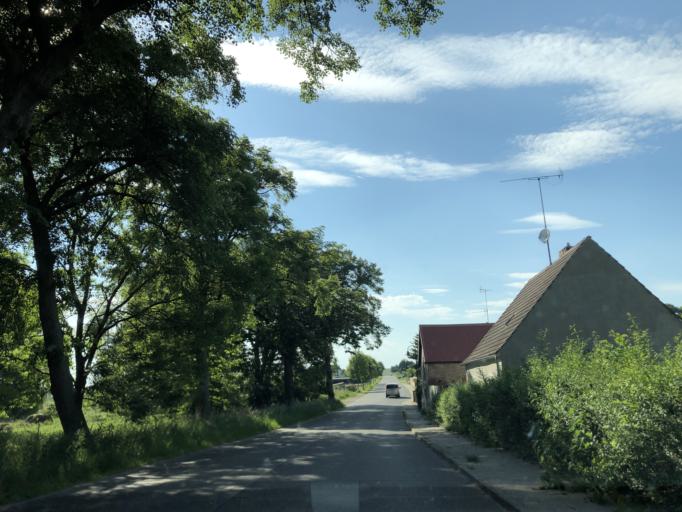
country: DE
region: Brandenburg
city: Angermunde
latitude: 53.0873
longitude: 13.9455
